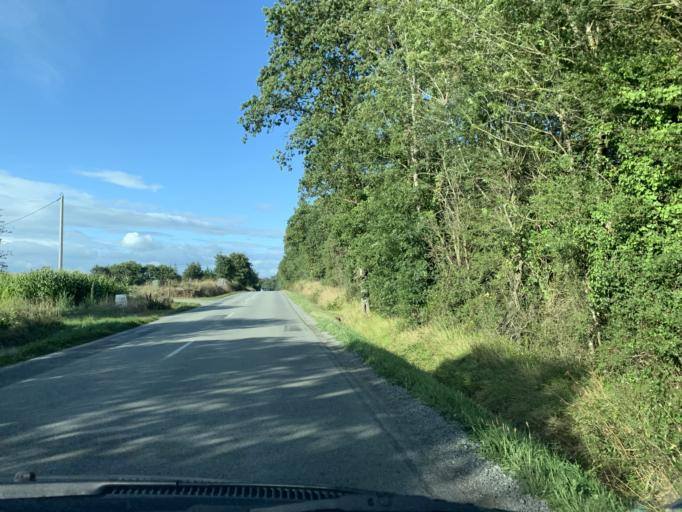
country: FR
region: Brittany
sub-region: Departement du Morbihan
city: Ferel
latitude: 47.4971
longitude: -2.3223
